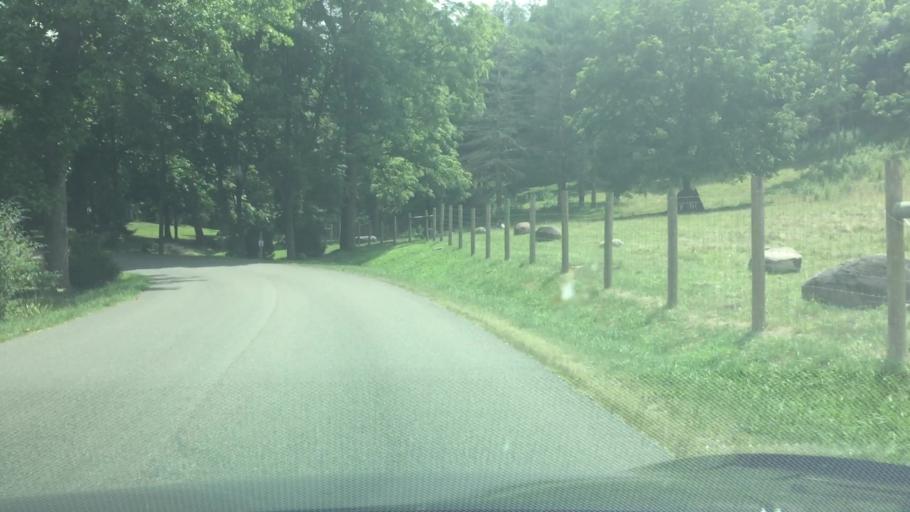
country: US
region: Virginia
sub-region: Wythe County
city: Wytheville
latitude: 36.9304
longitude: -81.0308
